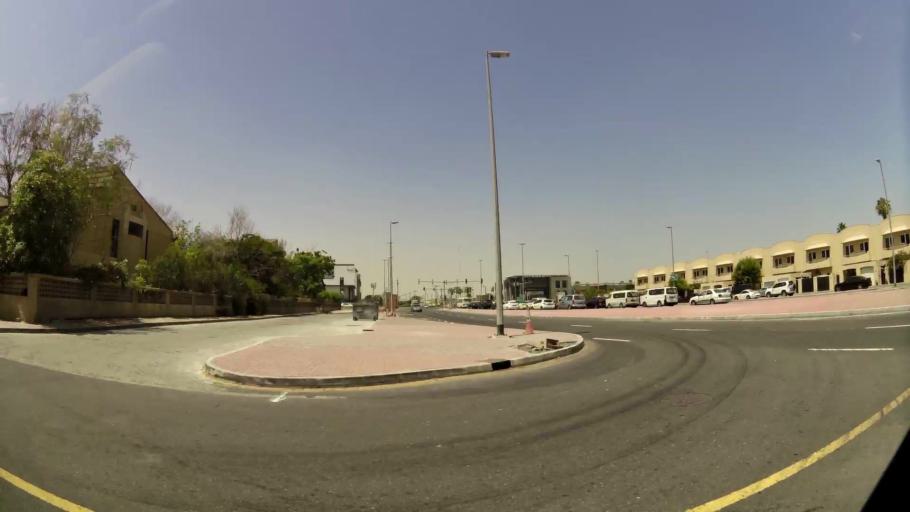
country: AE
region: Dubai
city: Dubai
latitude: 25.2110
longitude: 55.2619
